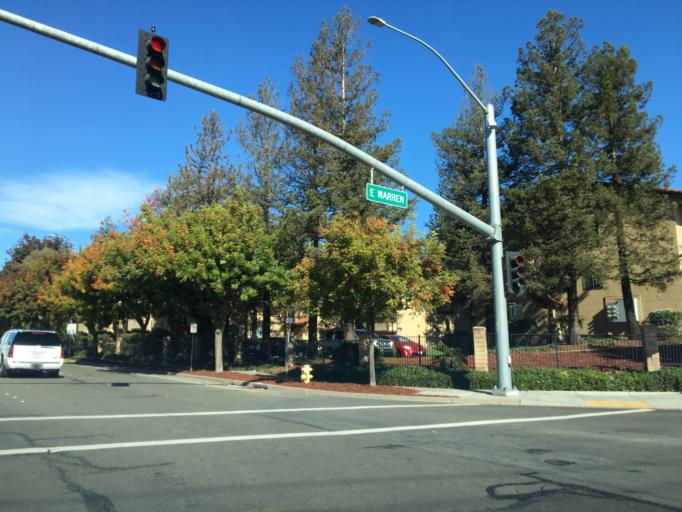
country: US
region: California
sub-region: Santa Clara County
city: Milpitas
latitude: 37.4871
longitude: -121.9279
